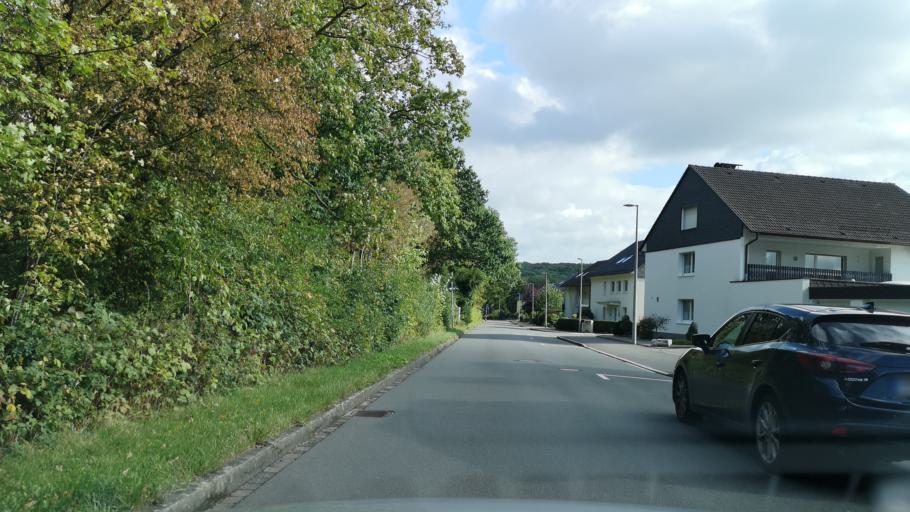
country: DE
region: North Rhine-Westphalia
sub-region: Regierungsbezirk Arnsberg
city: Menden
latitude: 51.4307
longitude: 7.7569
